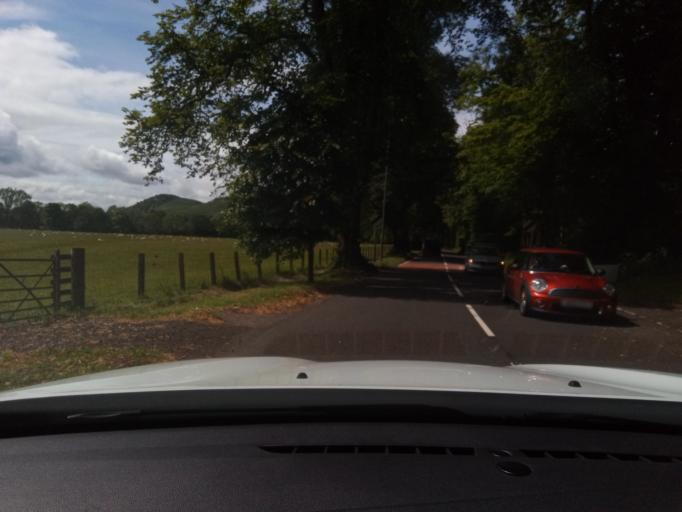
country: GB
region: Scotland
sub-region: Stirling
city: Callander
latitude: 56.2455
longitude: -4.2304
